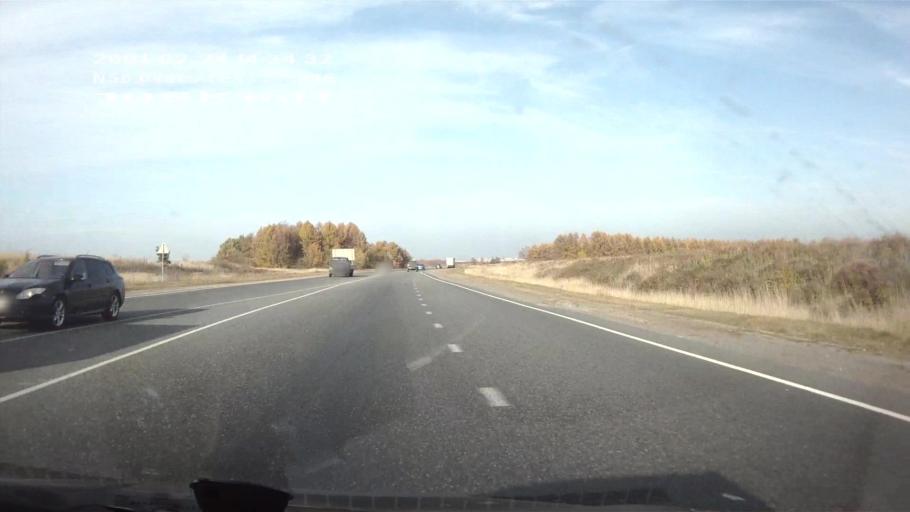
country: RU
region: Chuvashia
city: Kugesi
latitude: 56.0476
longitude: 47.3709
